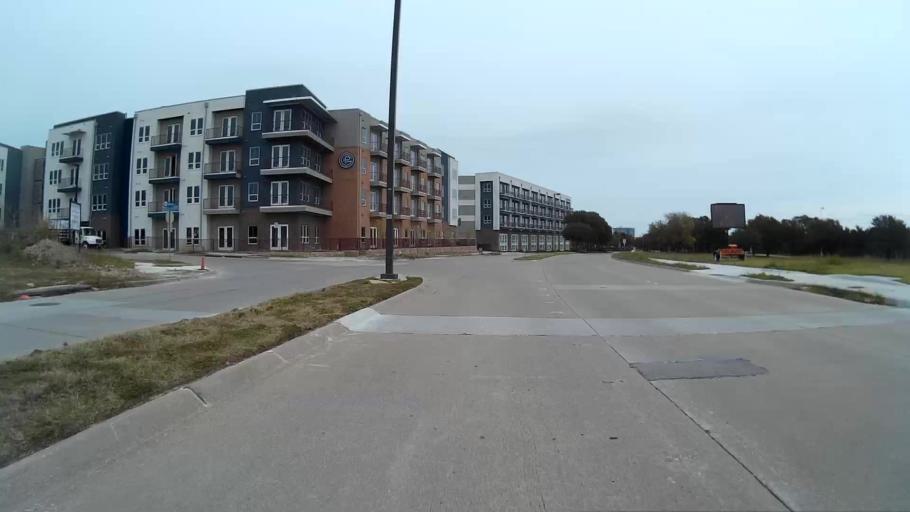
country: US
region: Texas
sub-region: Collin County
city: Plano
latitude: 32.9815
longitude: -96.7068
